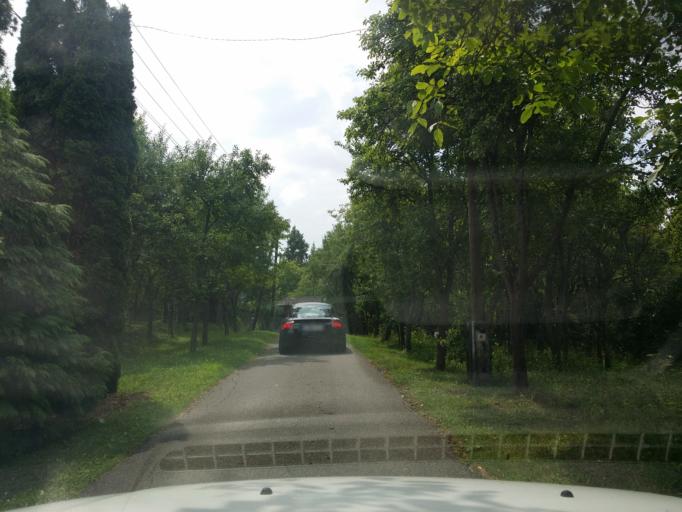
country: HU
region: Borsod-Abauj-Zemplen
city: Gonc
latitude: 48.4856
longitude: 21.3616
